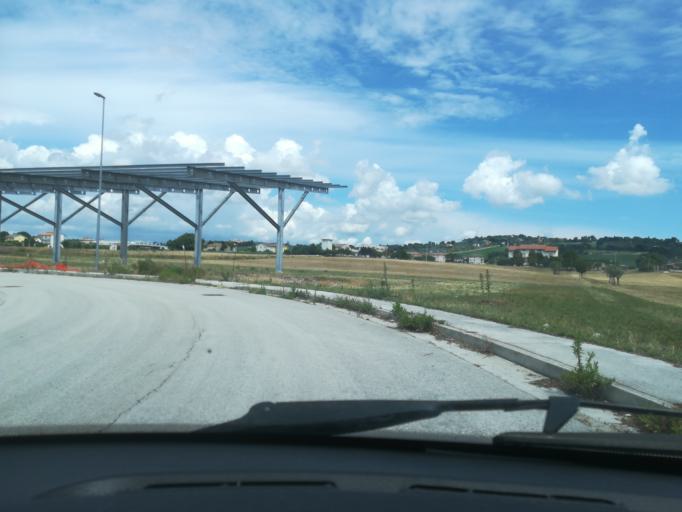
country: IT
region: The Marches
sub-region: Provincia di Macerata
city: Santa Maria Apparente
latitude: 43.2888
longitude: 13.6793
